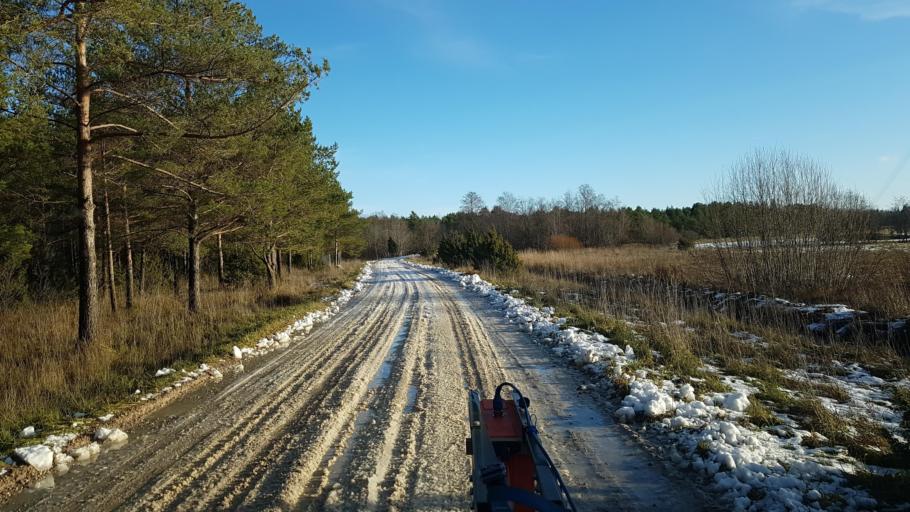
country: EE
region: Harju
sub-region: Keila linn
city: Keila
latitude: 59.2704
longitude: 24.2827
